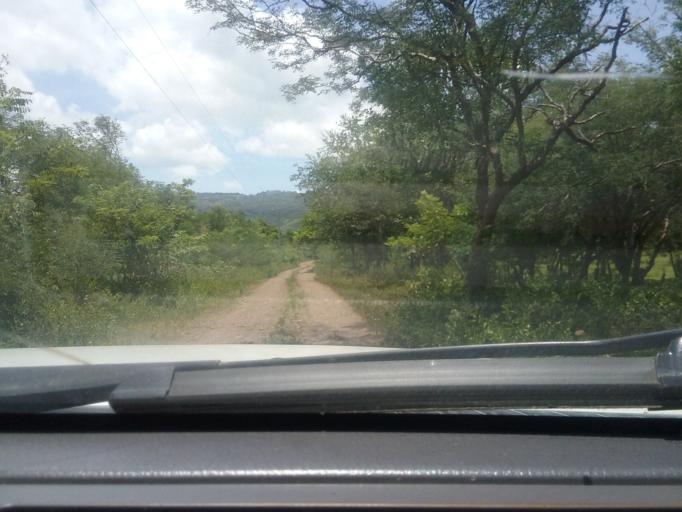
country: NI
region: Matagalpa
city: Terrabona
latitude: 12.6661
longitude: -85.9847
